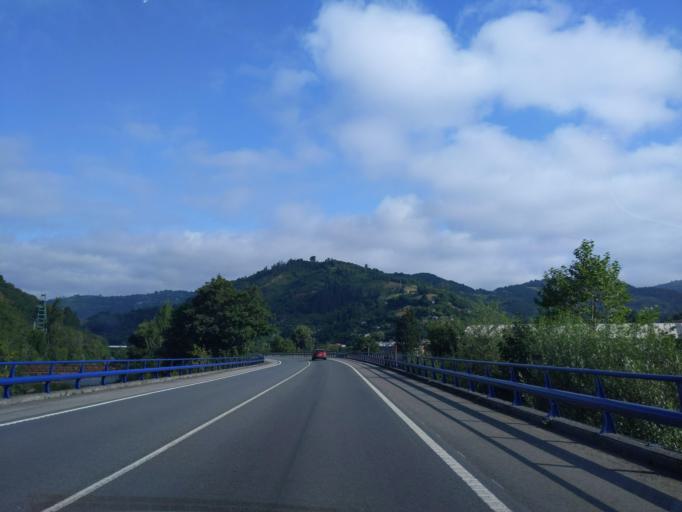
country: ES
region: Asturias
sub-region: Province of Asturias
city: Pola de Laviana
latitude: 43.2564
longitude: -5.5747
